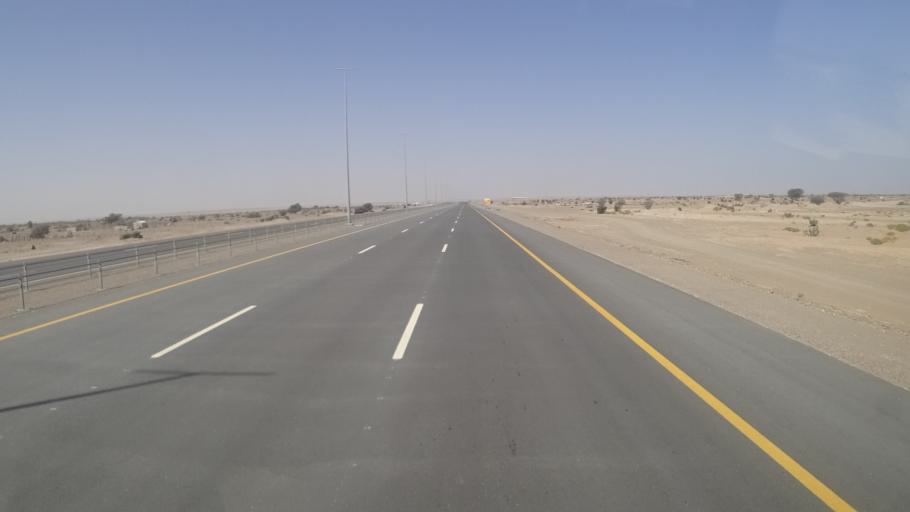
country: OM
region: Ash Sharqiyah
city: Badiyah
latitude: 22.2769
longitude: 59.1865
